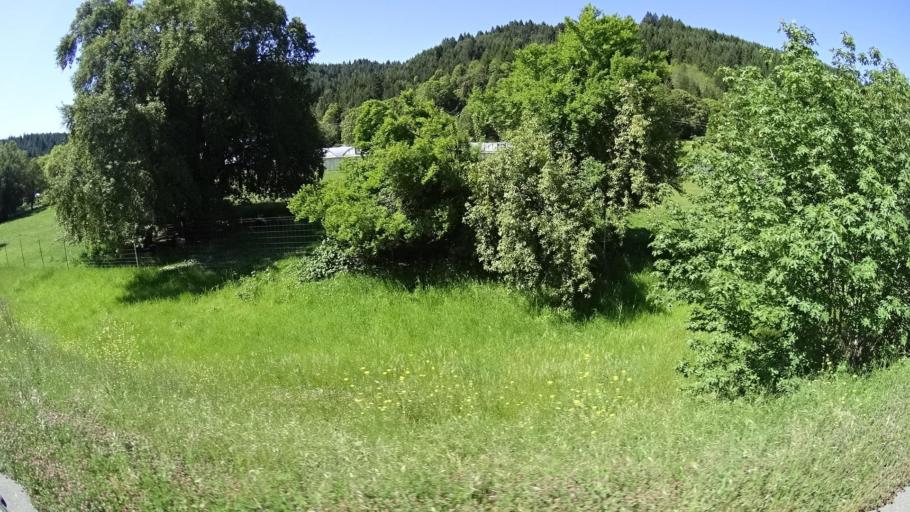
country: US
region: California
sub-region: Humboldt County
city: Rio Dell
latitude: 40.2366
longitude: -124.1194
